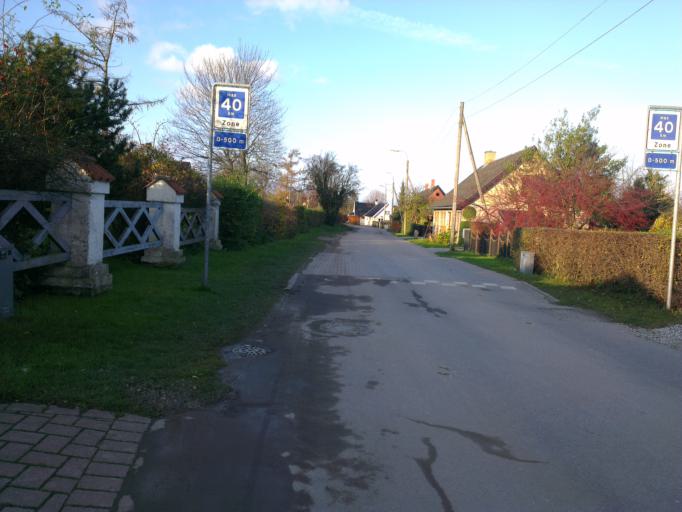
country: DK
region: Capital Region
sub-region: Frederikssund Kommune
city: Jaegerspris
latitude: 55.8559
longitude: 11.9987
